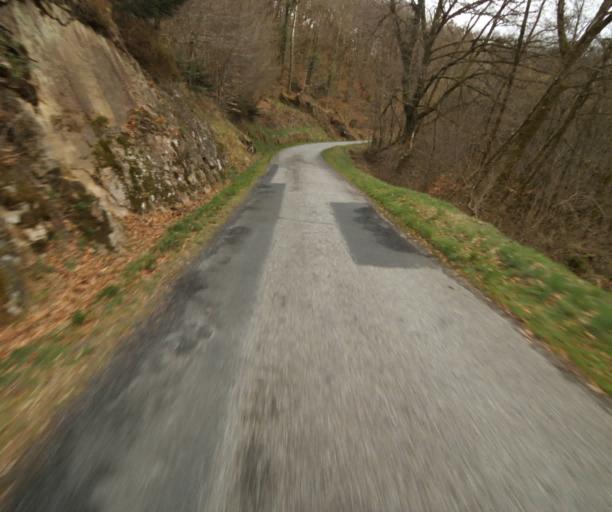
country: FR
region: Limousin
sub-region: Departement de la Correze
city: Argentat
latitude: 45.2306
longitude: 1.9880
